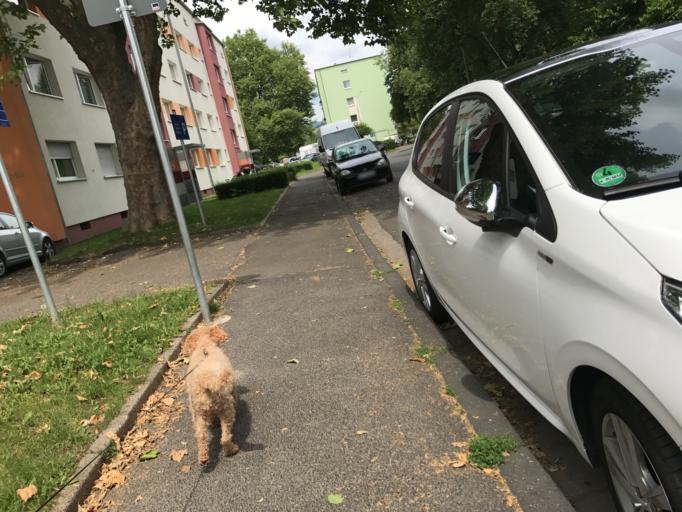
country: DE
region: Rheinland-Pfalz
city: Budenheim
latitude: 50.0461
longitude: 8.1863
